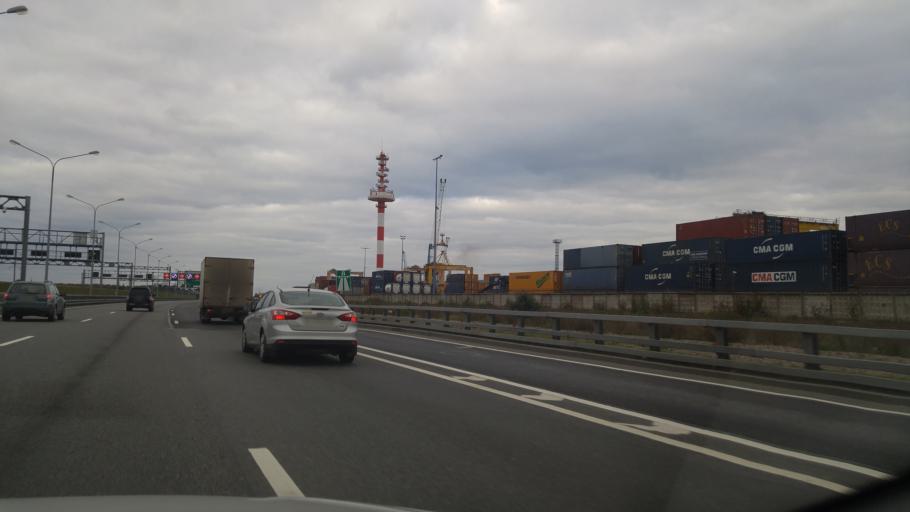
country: RU
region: St.-Petersburg
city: Kronshtadt
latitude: 60.0006
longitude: 29.7027
